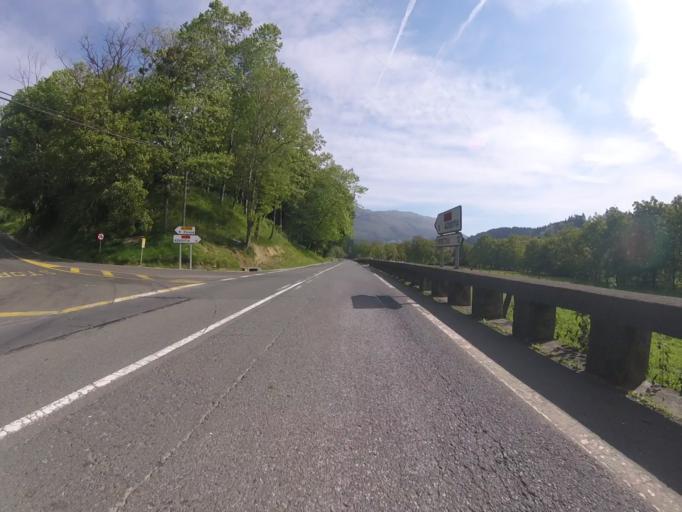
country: ES
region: Basque Country
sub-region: Provincia de Guipuzcoa
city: Azkoitia
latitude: 43.1657
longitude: -2.3300
